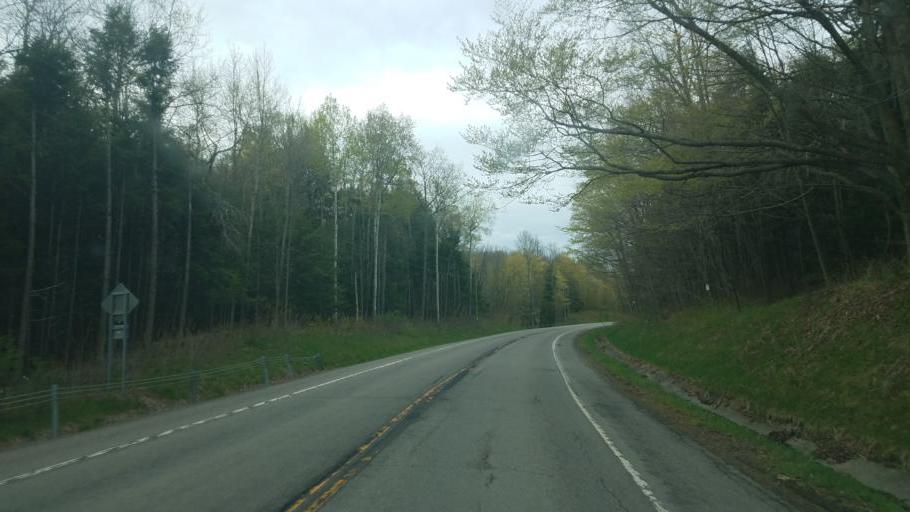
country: US
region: New York
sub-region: Steuben County
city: Canisteo
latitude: 42.1705
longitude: -77.5264
